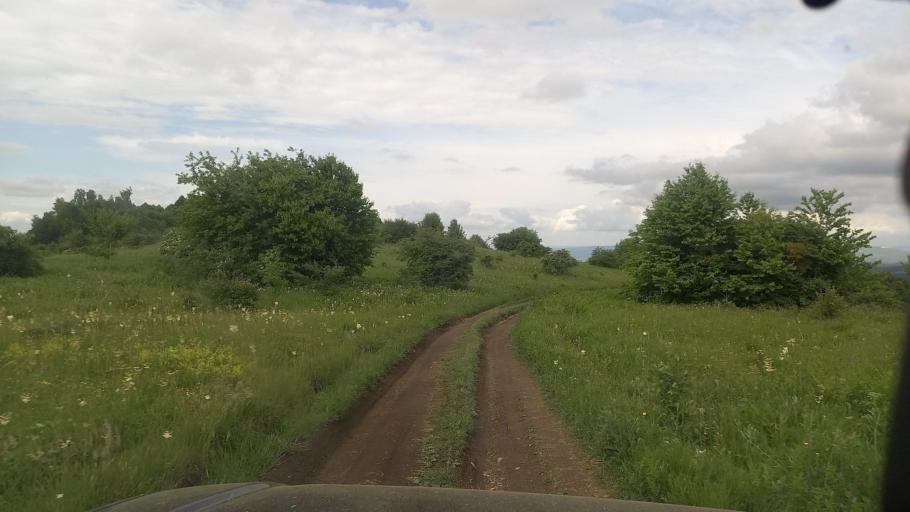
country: RU
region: Karachayevo-Cherkesiya
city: Pregradnaya
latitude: 44.0341
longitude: 41.3141
